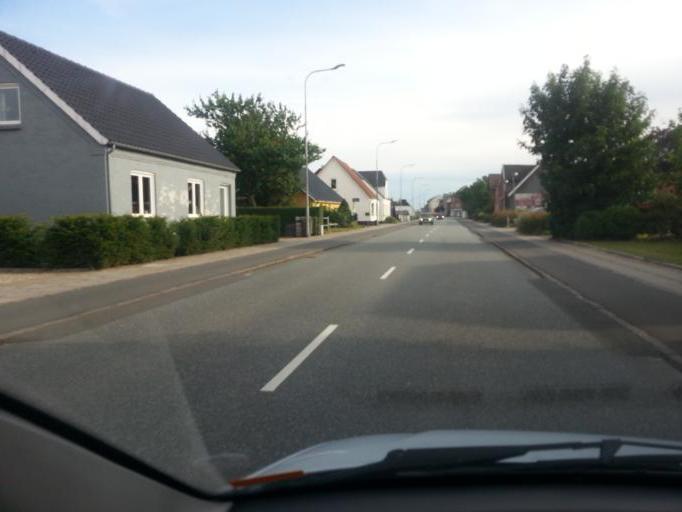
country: DK
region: South Denmark
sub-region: Vejen Kommune
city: Holsted
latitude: 55.4875
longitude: 8.9138
